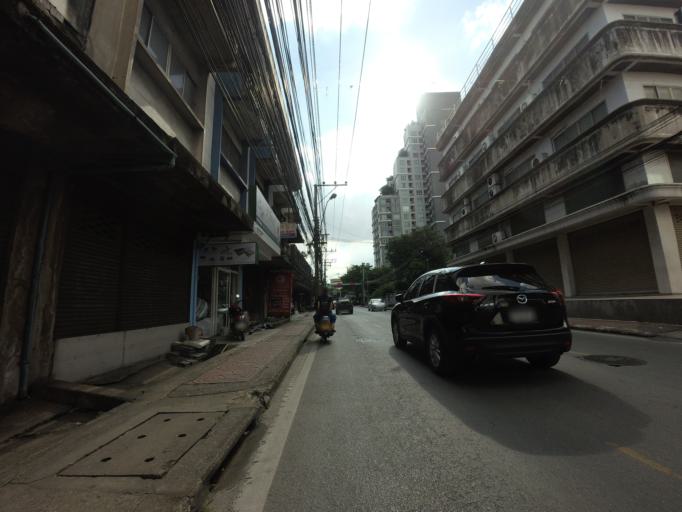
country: TH
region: Bangkok
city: Huai Khwang
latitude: 13.7786
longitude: 100.5754
